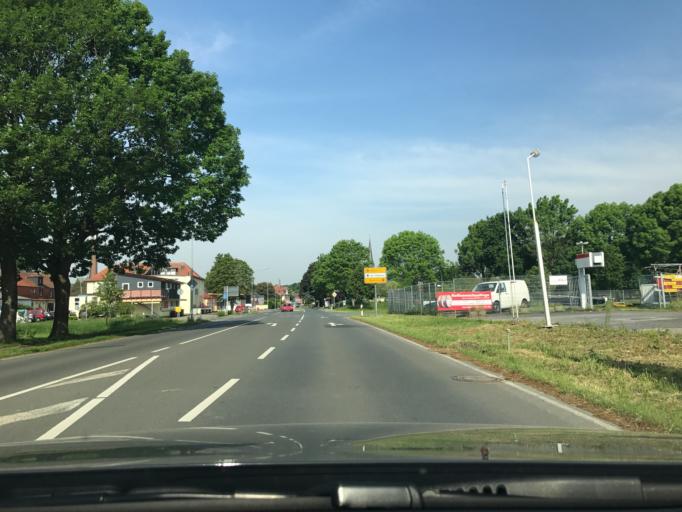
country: DE
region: North Rhine-Westphalia
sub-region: Regierungsbezirk Dusseldorf
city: Rheurdt
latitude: 51.4409
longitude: 6.4918
